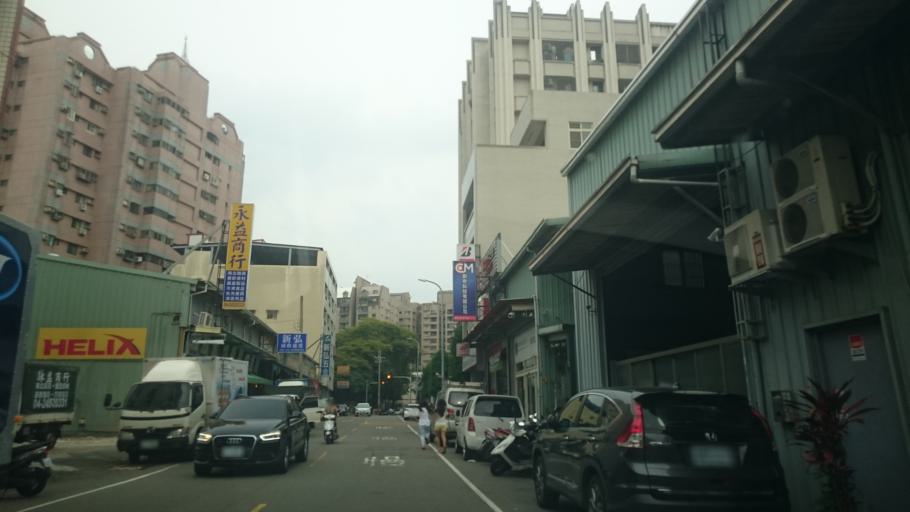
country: TW
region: Taiwan
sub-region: Taichung City
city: Taichung
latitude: 24.1772
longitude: 120.6387
